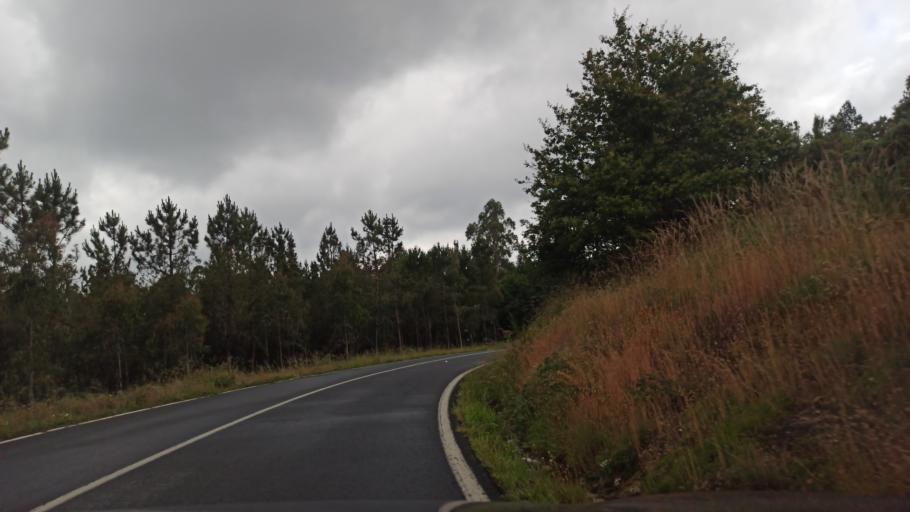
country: ES
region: Galicia
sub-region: Provincia da Coruna
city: Santiso
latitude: 42.7844
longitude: -8.0708
